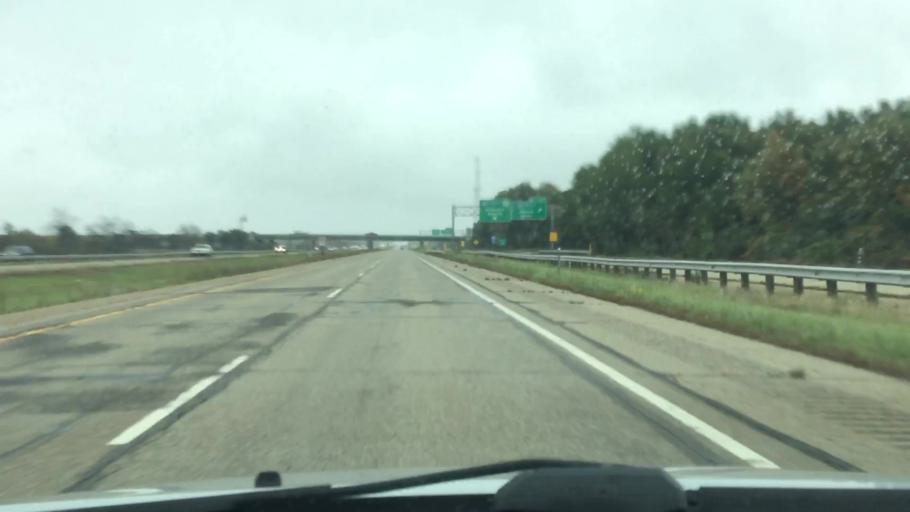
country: US
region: Wisconsin
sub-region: Walworth County
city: Elkhorn
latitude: 42.6779
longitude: -88.5245
